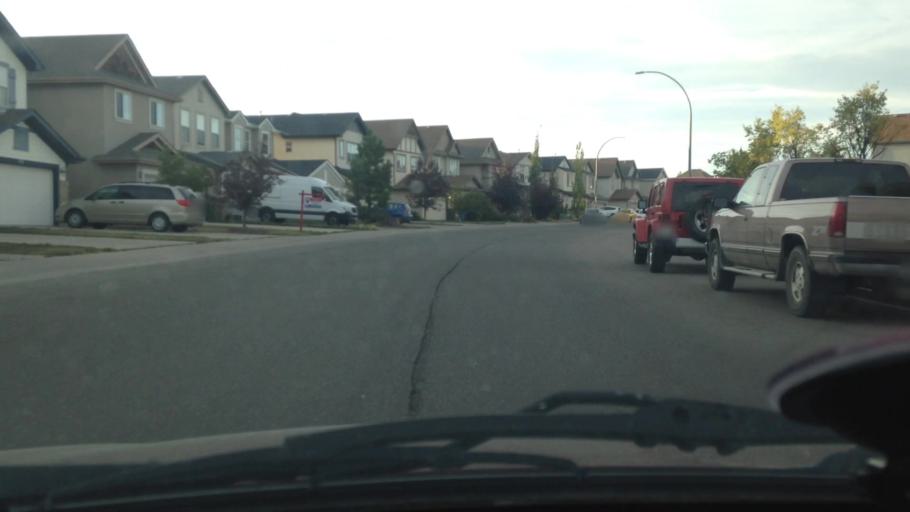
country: CA
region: Alberta
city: Calgary
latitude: 51.1652
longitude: -114.1210
